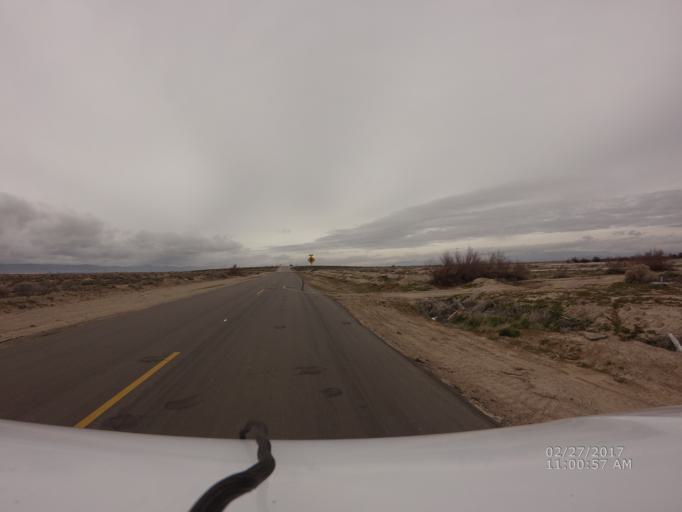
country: US
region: California
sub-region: Los Angeles County
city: Lancaster
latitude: 34.7479
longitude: -118.1647
